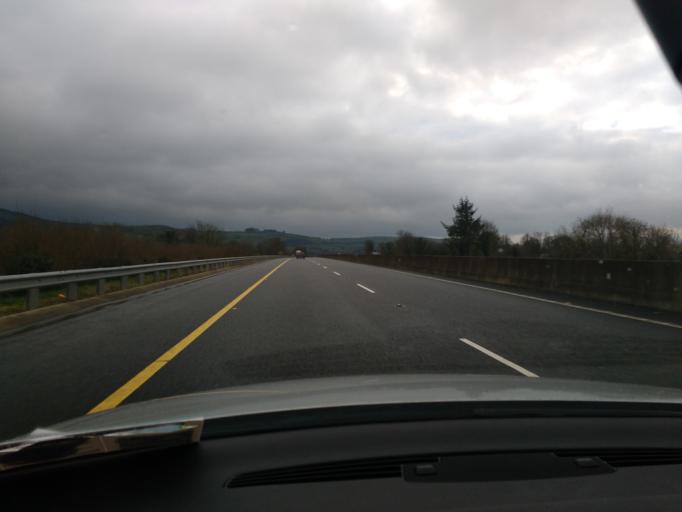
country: IE
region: Munster
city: Ballina
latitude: 52.8082
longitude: -8.3136
